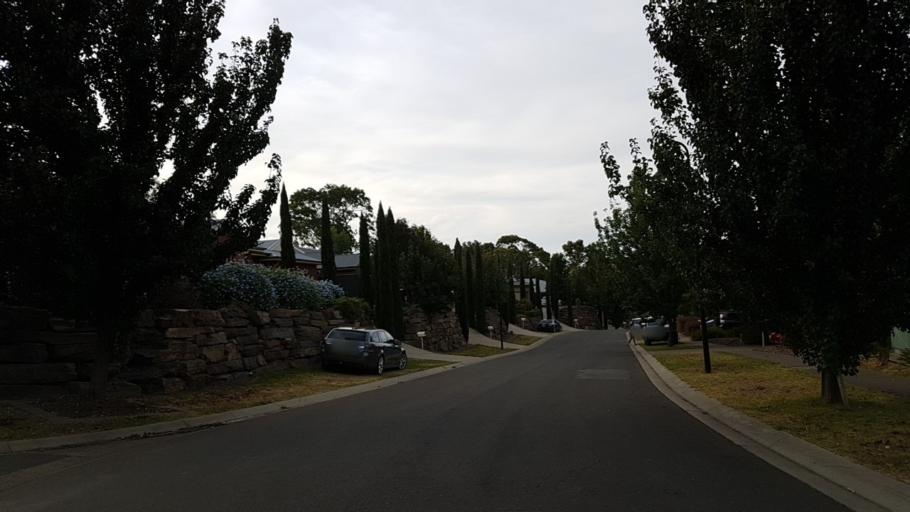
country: AU
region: South Australia
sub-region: Mount Barker
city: Nairne
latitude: -35.0261
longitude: 138.9090
